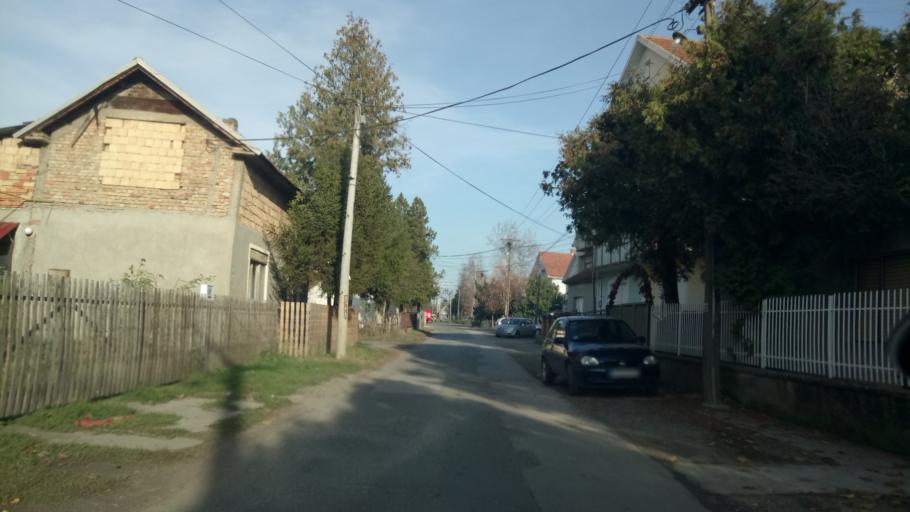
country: RS
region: Autonomna Pokrajina Vojvodina
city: Nova Pazova
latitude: 44.9514
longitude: 20.2244
